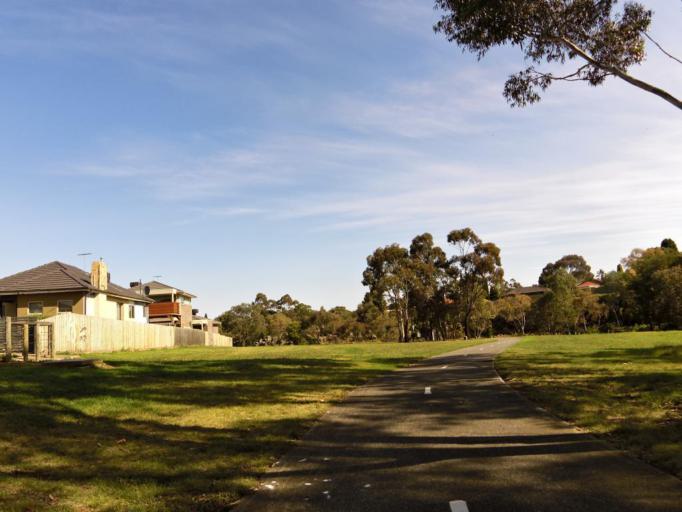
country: AU
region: Victoria
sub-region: Brimbank
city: Sunshine West
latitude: -37.7957
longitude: 144.8223
